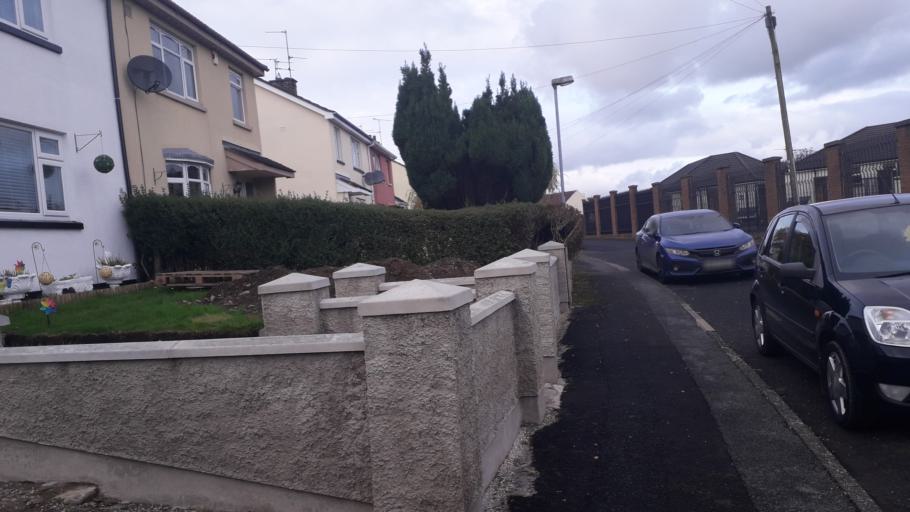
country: GB
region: Northern Ireland
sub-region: City of Derry
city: Derry
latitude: 55.0046
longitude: -7.3270
